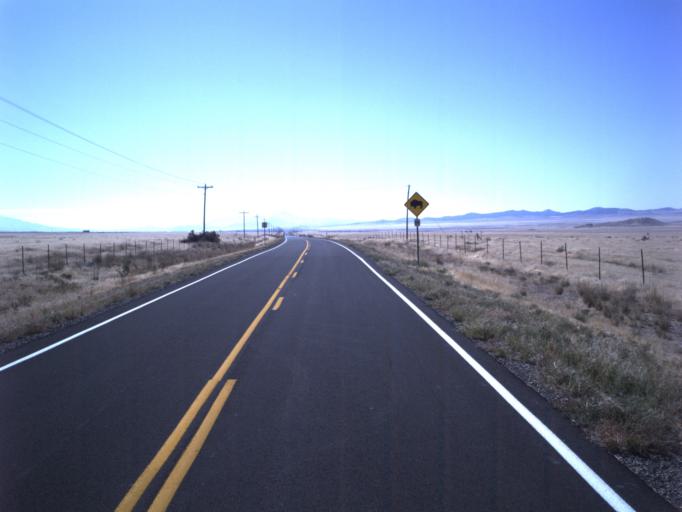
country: US
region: Utah
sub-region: Tooele County
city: Grantsville
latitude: 40.4189
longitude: -112.7488
